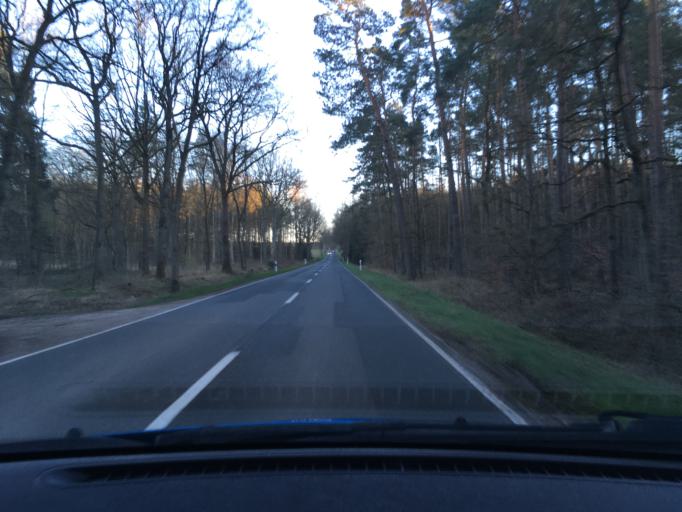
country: DE
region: Lower Saxony
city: Bleckede
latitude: 53.2531
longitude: 10.7451
